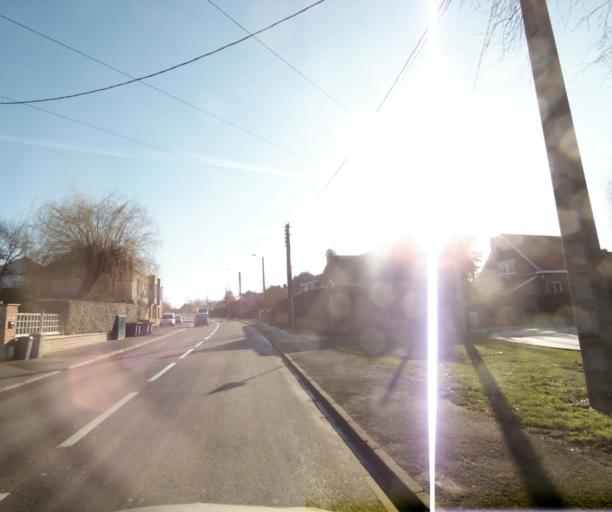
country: FR
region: Nord-Pas-de-Calais
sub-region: Departement du Nord
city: Marly
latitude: 50.3397
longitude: 3.5508
